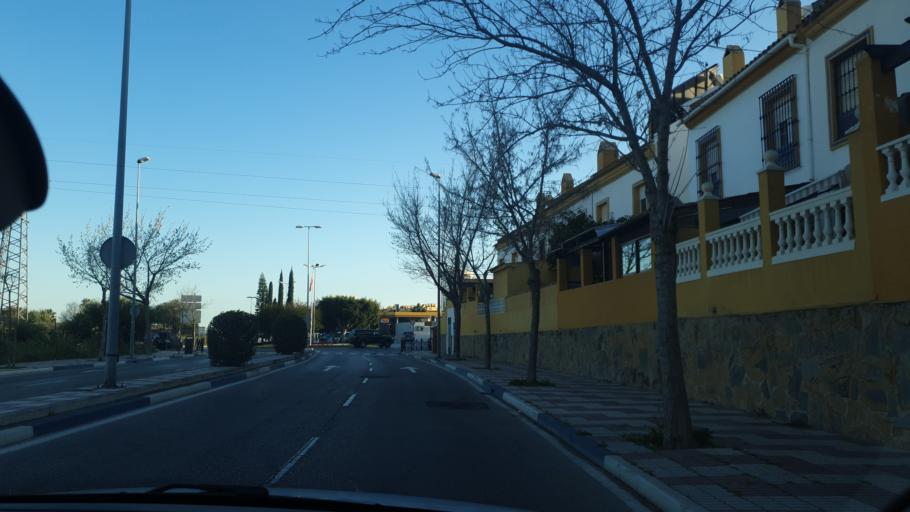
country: ES
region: Andalusia
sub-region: Provincia de Malaga
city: Marbella
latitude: 36.5212
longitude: -4.8920
